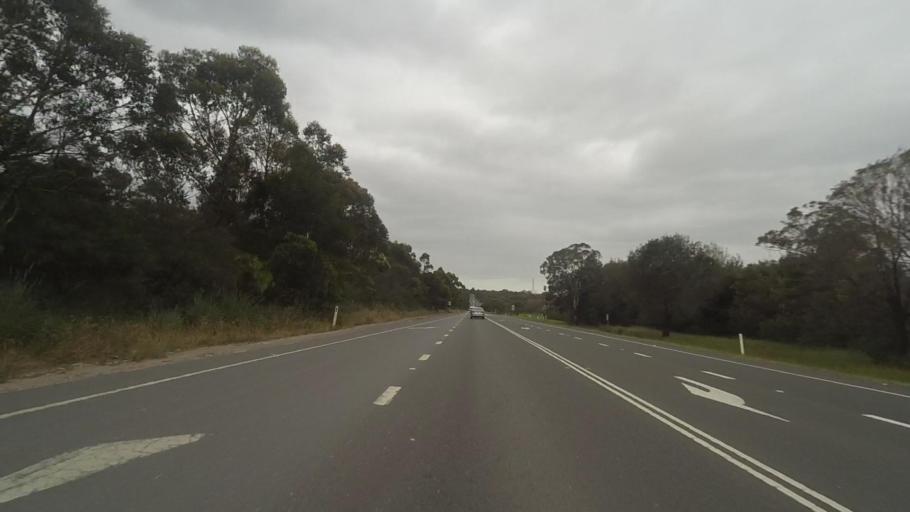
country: AU
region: New South Wales
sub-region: Sutherland Shire
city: Engadine
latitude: -34.0484
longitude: 150.9805
